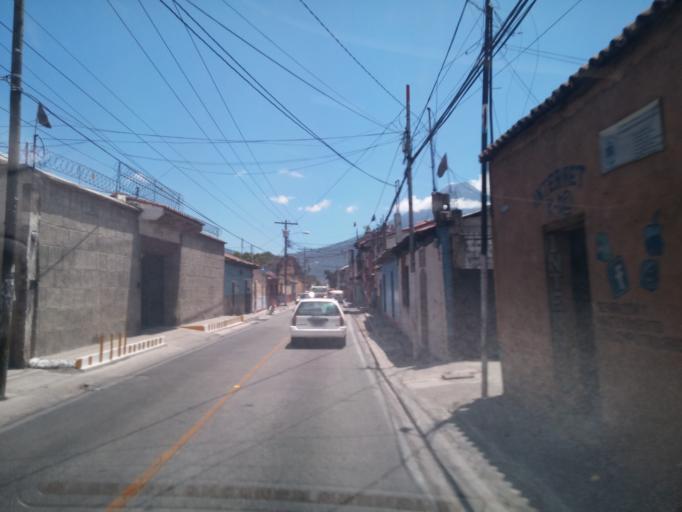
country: GT
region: Sacatepequez
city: Jocotenango
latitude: 14.5765
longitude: -90.7423
